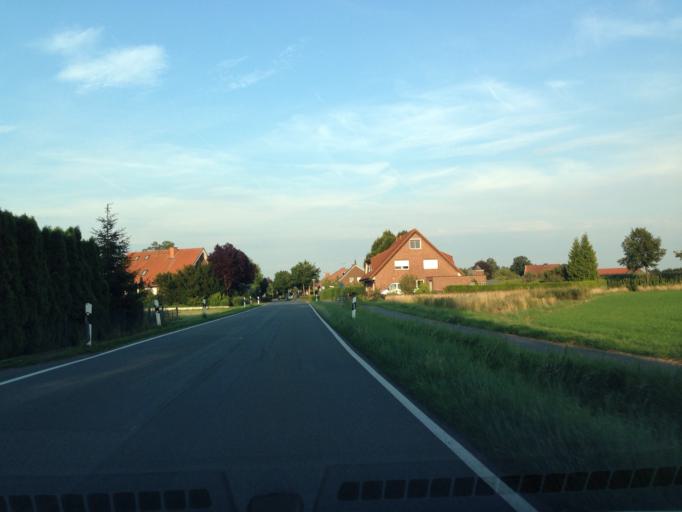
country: DE
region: North Rhine-Westphalia
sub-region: Regierungsbezirk Munster
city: Senden
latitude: 51.8247
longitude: 7.5278
